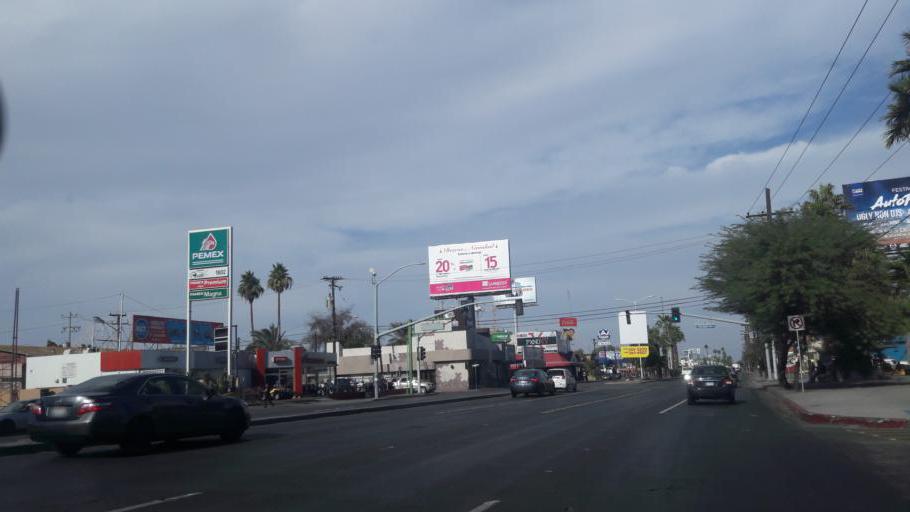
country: MX
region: Baja California
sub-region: Mexicali
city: Mexicali
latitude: 32.6483
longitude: -115.4522
